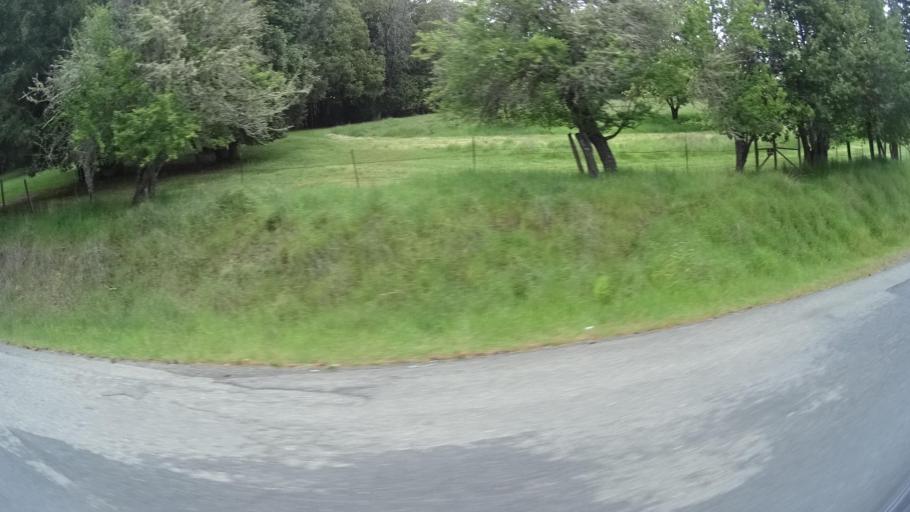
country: US
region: California
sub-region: Humboldt County
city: Redway
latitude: 40.2860
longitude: -123.8002
